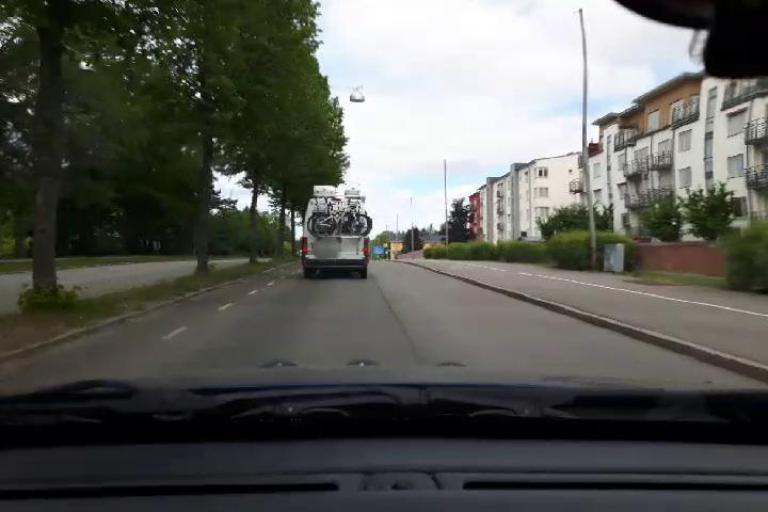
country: SE
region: Uppsala
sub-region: Uppsala Kommun
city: Gamla Uppsala
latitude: 59.8778
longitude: 17.6233
